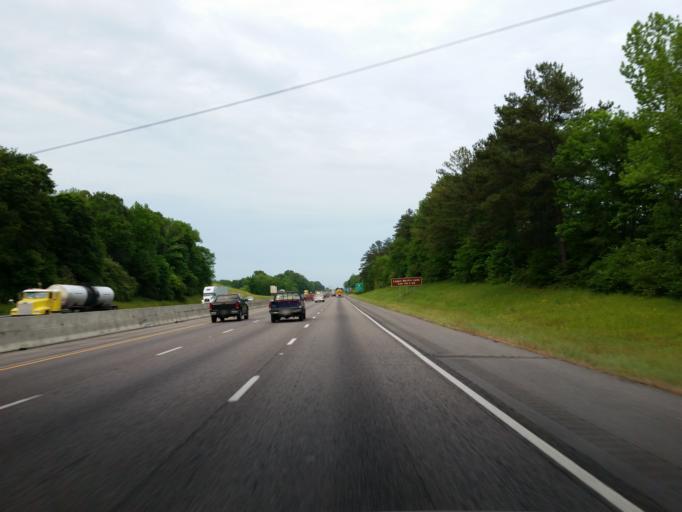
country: US
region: Alabama
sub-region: Saint Clair County
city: Pell City
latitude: 33.6023
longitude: -86.3059
